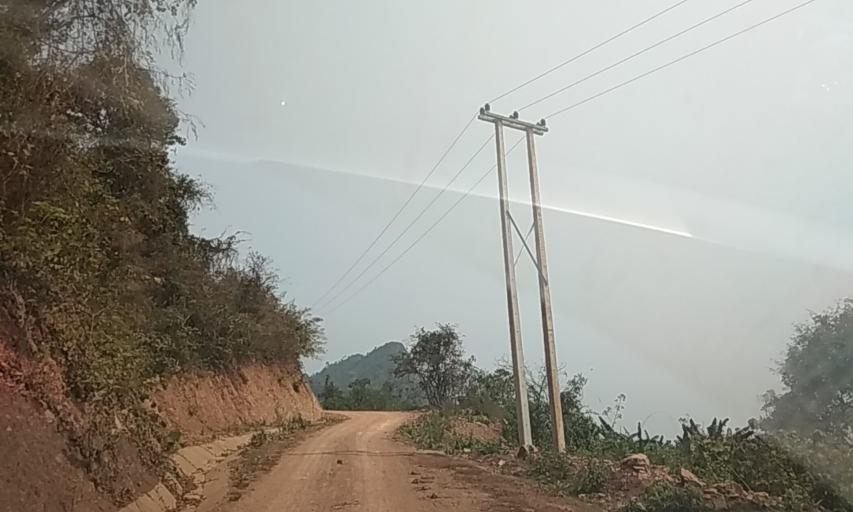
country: VN
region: Huyen Dien Bien
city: Dien Bien Phu
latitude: 21.4489
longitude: 102.7671
